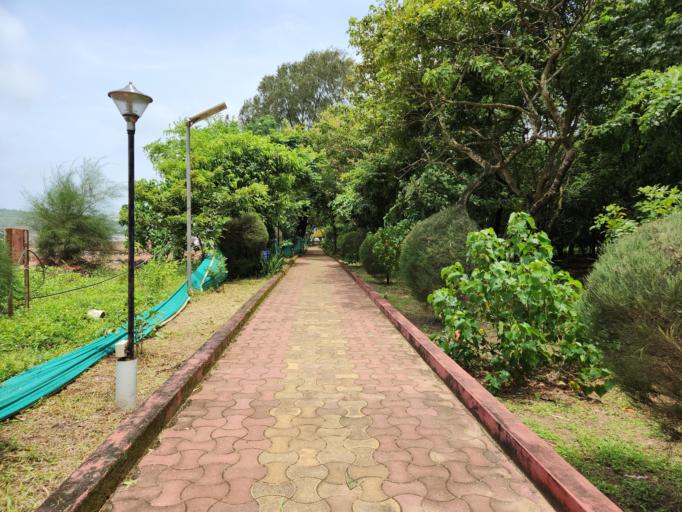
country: IN
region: Goa
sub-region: North Goa
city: Panaji
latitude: 15.4979
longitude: 73.8183
